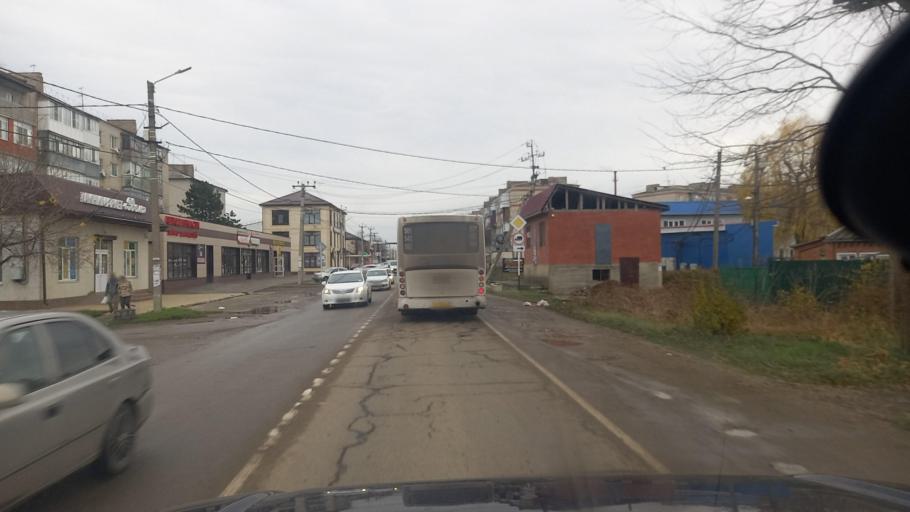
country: RU
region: Adygeya
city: Yablonovskiy
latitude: 44.9800
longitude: 38.9342
